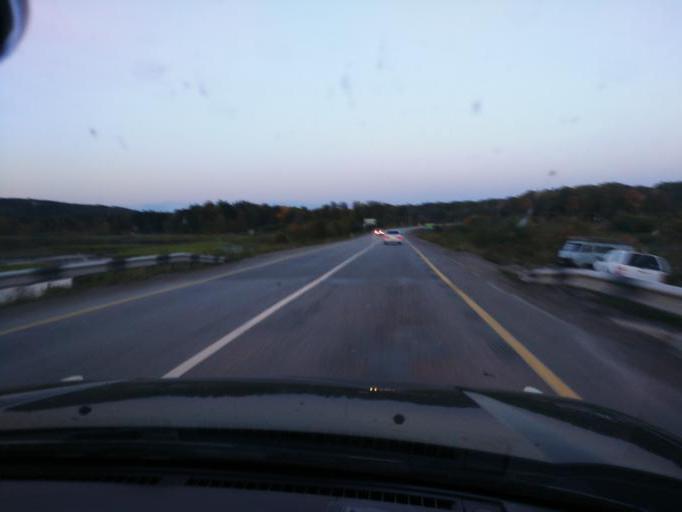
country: RU
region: Perm
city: Verkhnechusovskiye Gorodki
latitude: 58.2936
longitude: 56.8838
